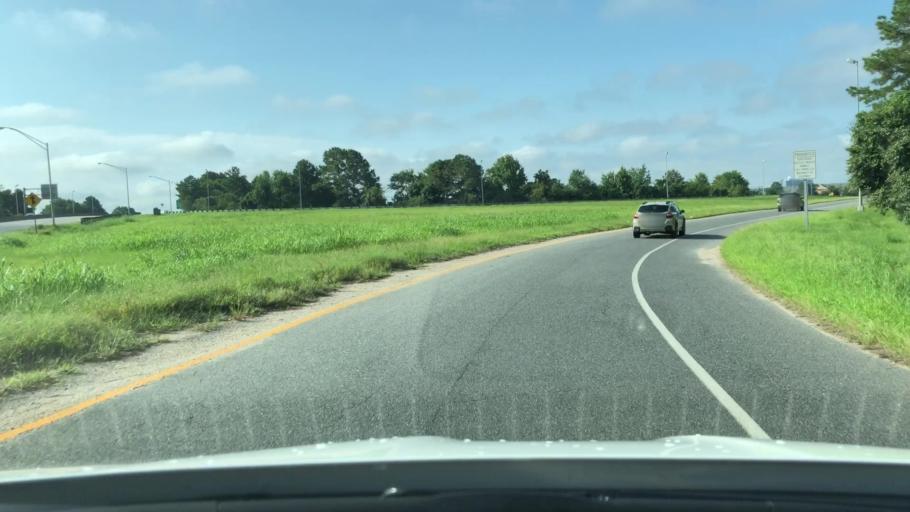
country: US
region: Virginia
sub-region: City of Chesapeake
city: Chesapeake
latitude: 36.7873
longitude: -76.2354
